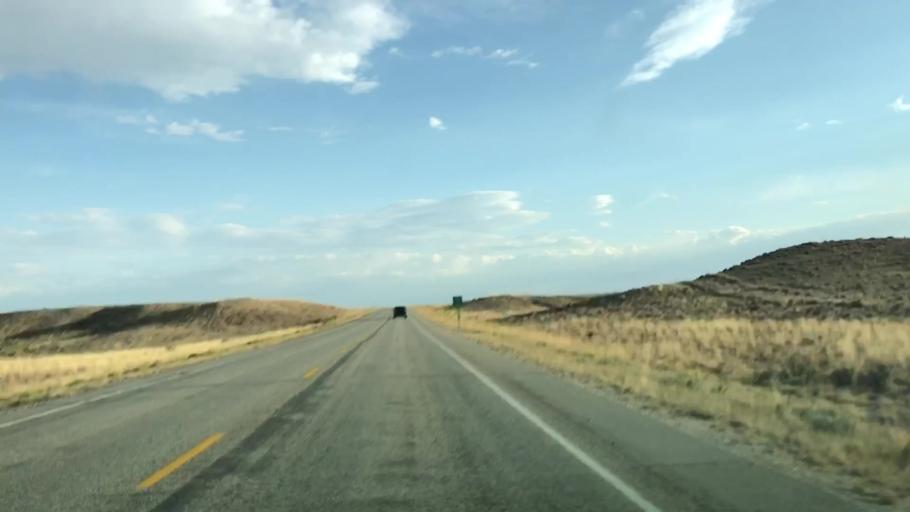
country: US
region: Wyoming
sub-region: Sublette County
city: Pinedale
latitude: 42.3468
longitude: -109.5220
